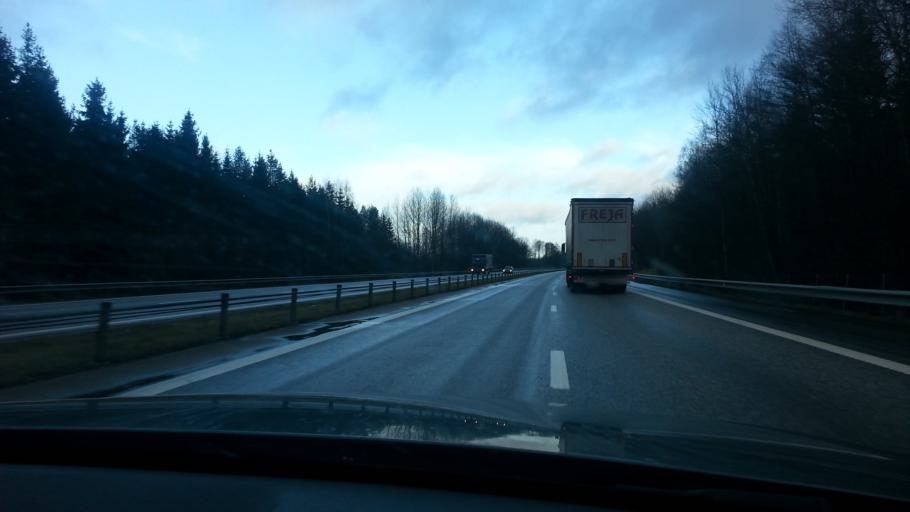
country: SE
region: OEstergoetland
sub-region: Odeshogs Kommun
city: OEdeshoeg
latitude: 58.1660
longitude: 14.5832
